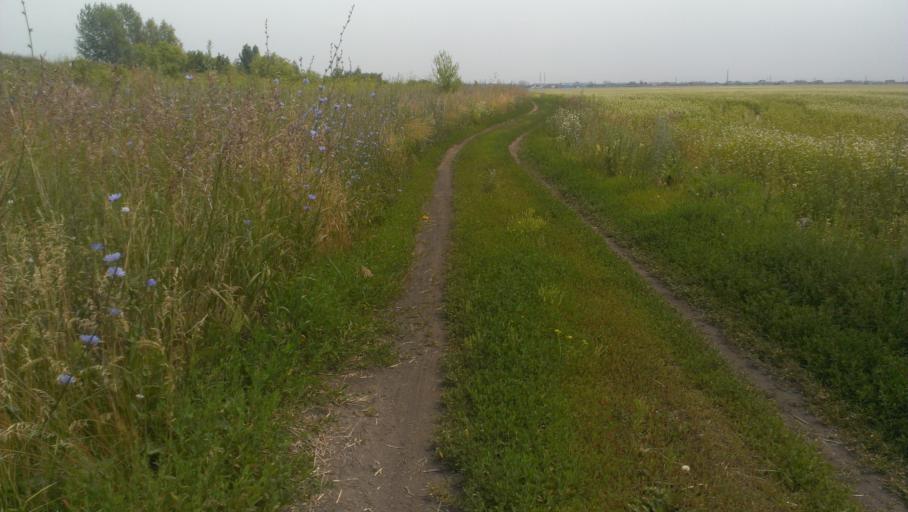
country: RU
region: Altai Krai
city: Gon'ba
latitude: 53.3798
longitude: 83.6330
